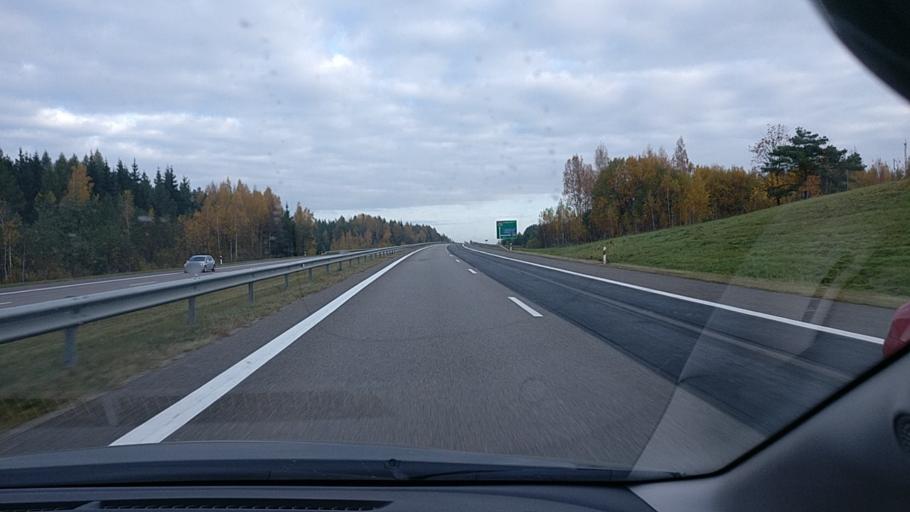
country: LT
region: Vilnius County
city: Ukmerge
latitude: 55.2204
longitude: 24.8167
